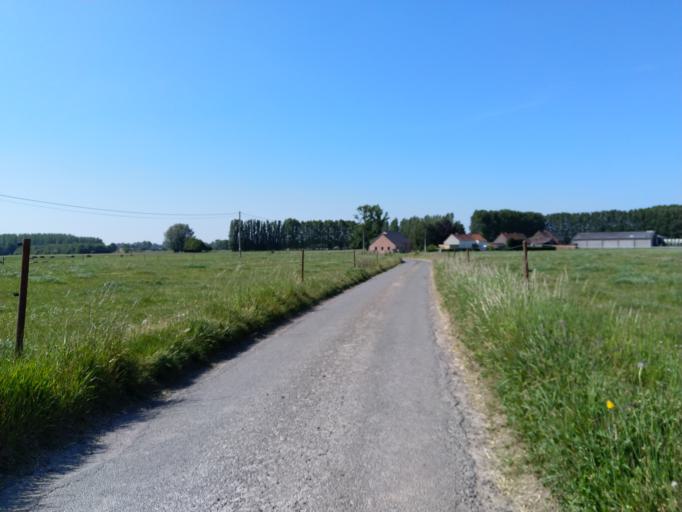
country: BE
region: Wallonia
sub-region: Province du Hainaut
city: Lens
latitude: 50.5474
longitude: 3.8722
